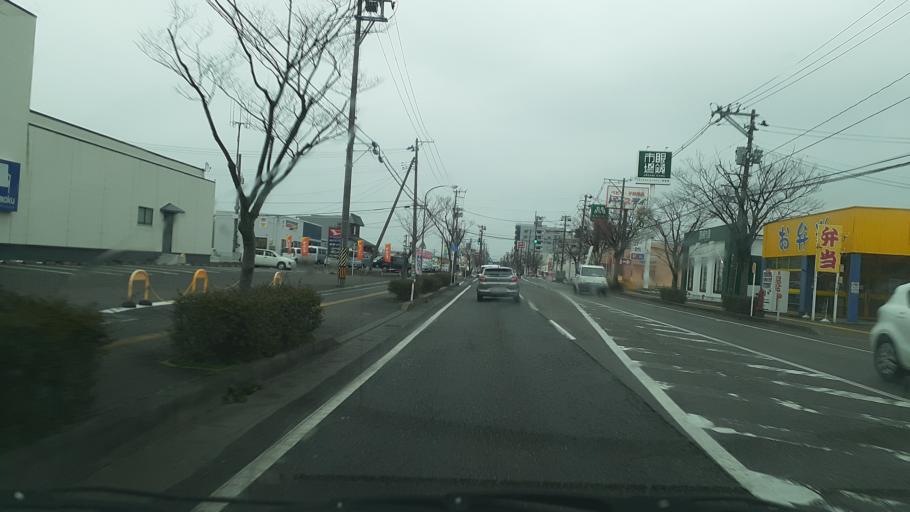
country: JP
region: Niigata
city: Kameda-honcho
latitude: 37.8735
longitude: 139.0987
